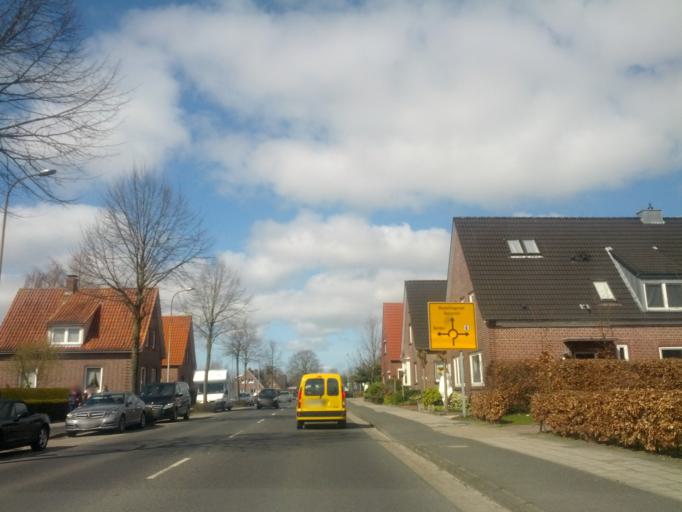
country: DE
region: Lower Saxony
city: Esens
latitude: 53.6440
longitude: 7.6095
